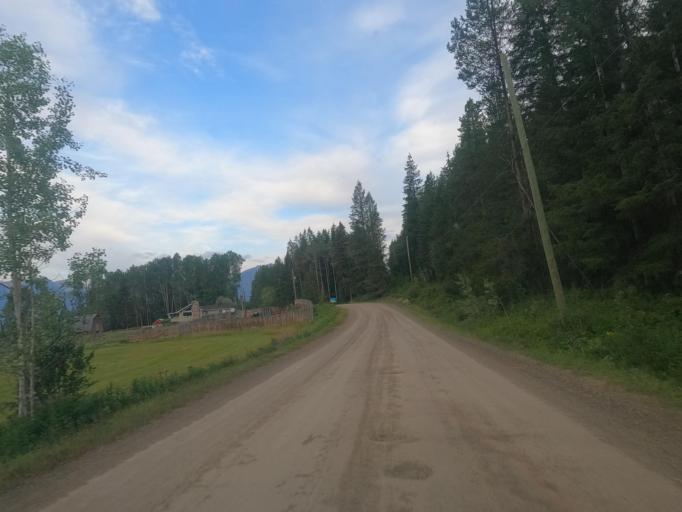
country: CA
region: British Columbia
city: Golden
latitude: 51.4457
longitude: -117.0222
